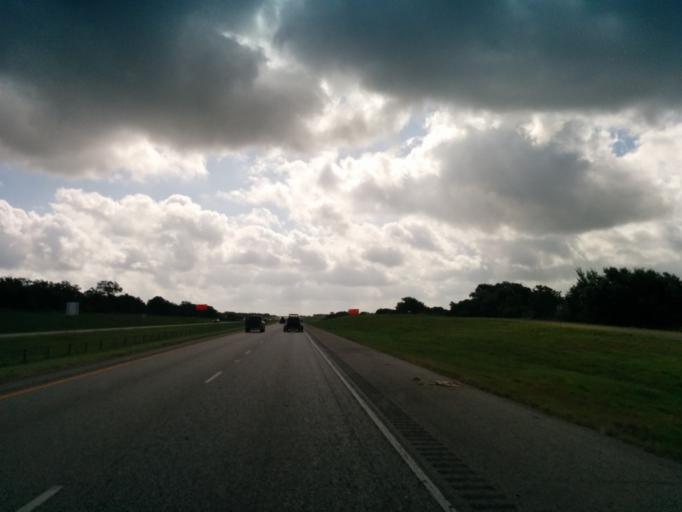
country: US
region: Texas
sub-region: Gonzales County
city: Waelder
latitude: 29.6628
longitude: -97.3779
